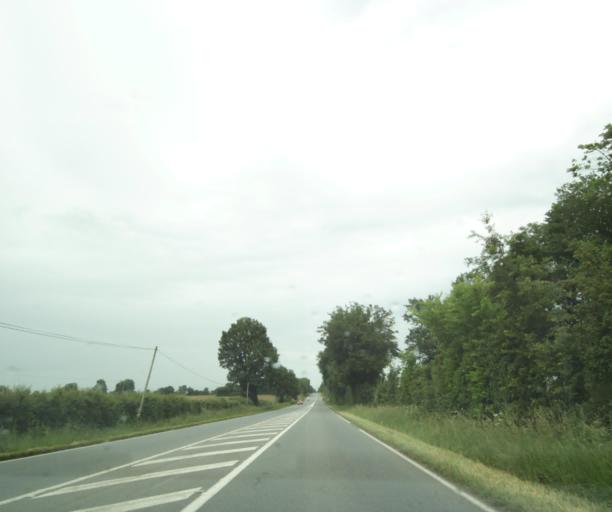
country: FR
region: Poitou-Charentes
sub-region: Departement des Deux-Sevres
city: Le Tallud
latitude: 46.6002
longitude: -0.2882
